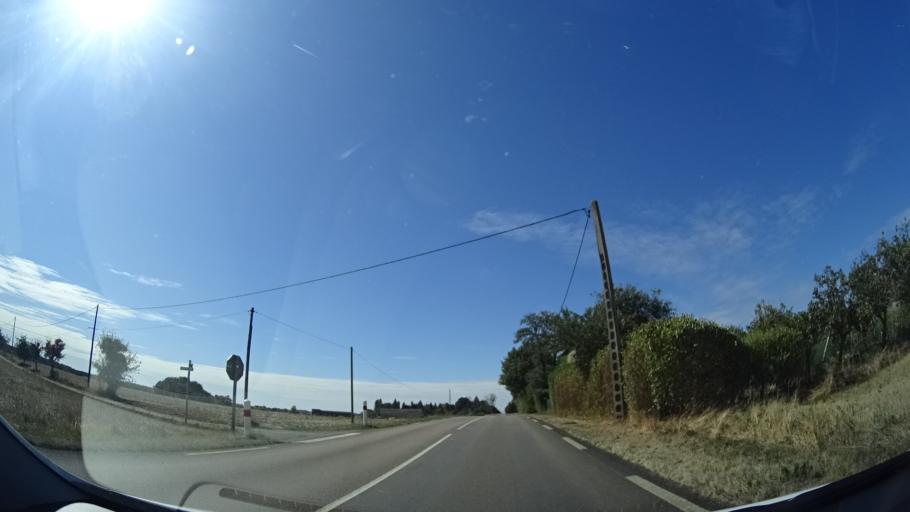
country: FR
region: Bourgogne
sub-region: Departement de l'Yonne
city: Charny
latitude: 47.9341
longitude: 3.1615
